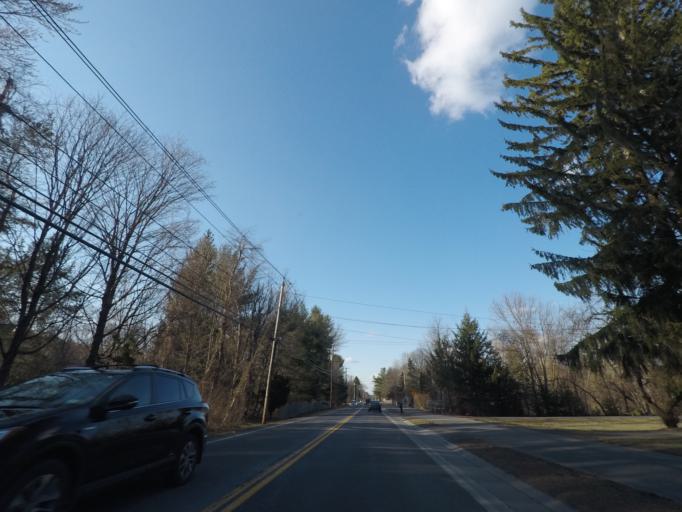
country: US
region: New York
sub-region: Saratoga County
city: Country Knolls
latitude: 42.8493
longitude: -73.7942
